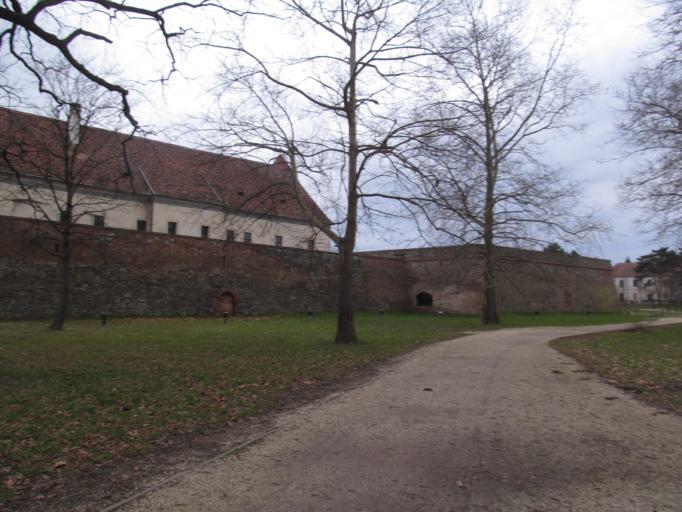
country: HU
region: Vas
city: Sarvar
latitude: 47.2520
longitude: 16.9385
